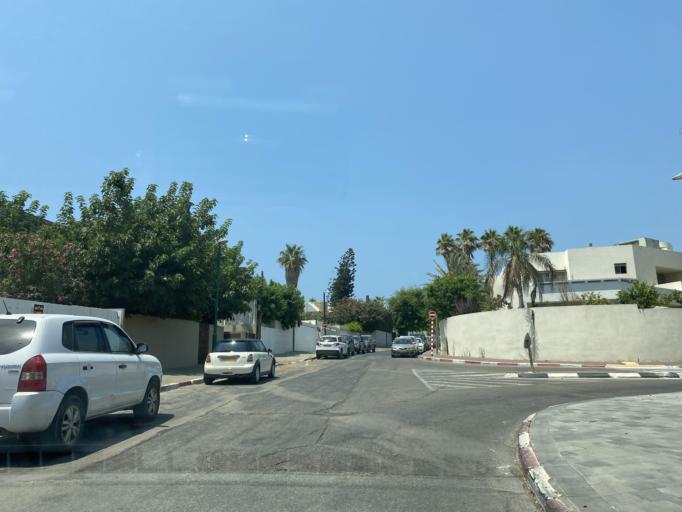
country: IL
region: Tel Aviv
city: Herzliya Pituah
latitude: 32.1802
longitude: 34.8041
